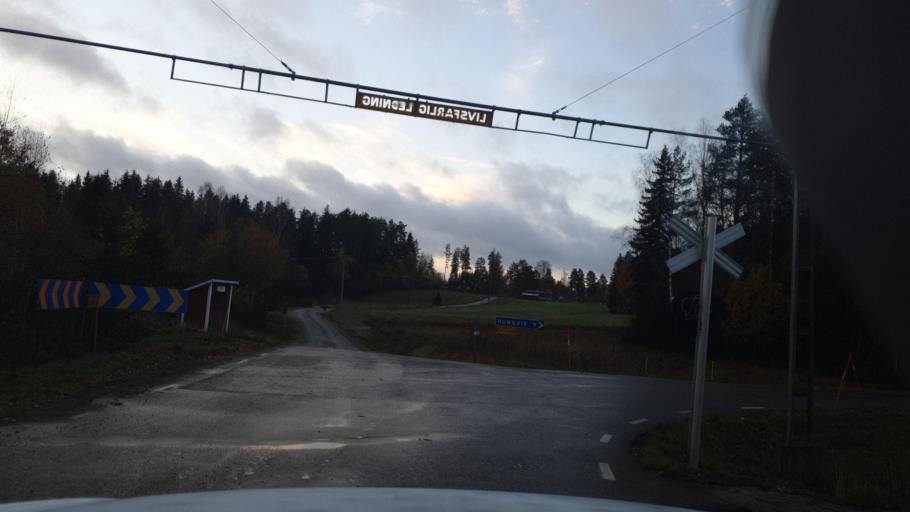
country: SE
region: Vaermland
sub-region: Arvika Kommun
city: Arvika
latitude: 59.6281
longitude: 12.8017
